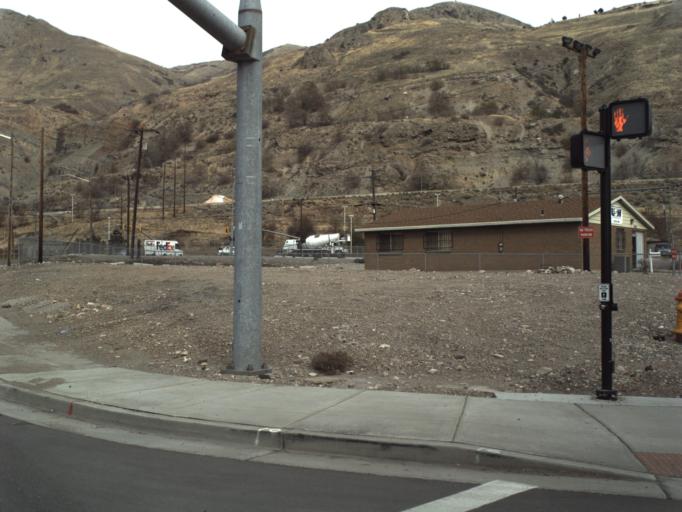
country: US
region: Utah
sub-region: Salt Lake County
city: Salt Lake City
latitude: 40.7890
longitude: -111.9024
